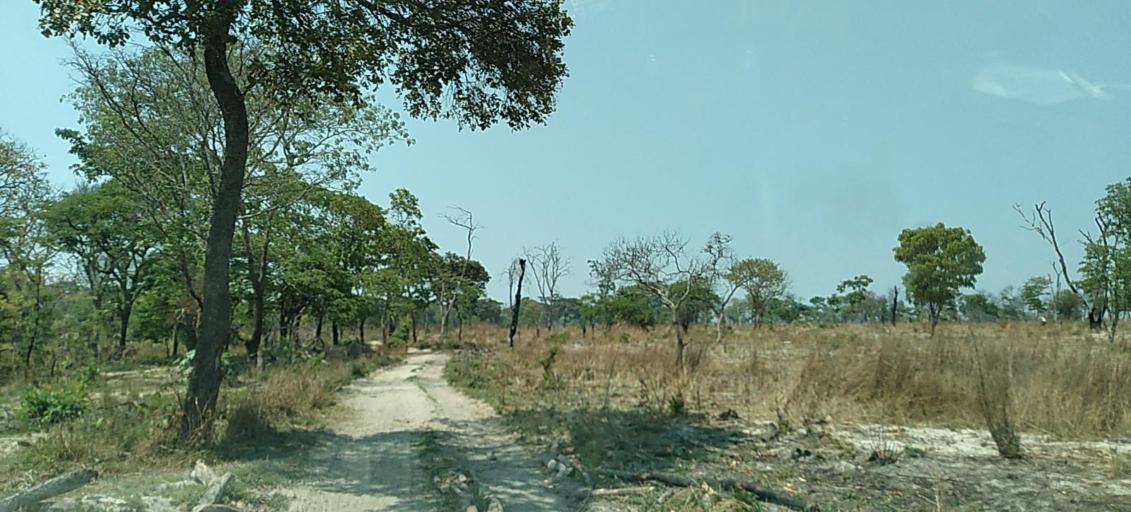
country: ZM
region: Copperbelt
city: Mpongwe
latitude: -13.8542
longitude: 28.0570
